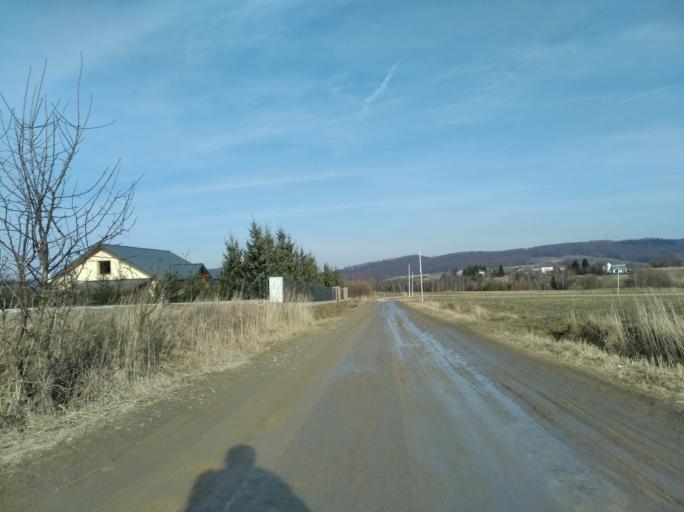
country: PL
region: Subcarpathian Voivodeship
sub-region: Powiat brzozowski
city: Grabownica Starzenska
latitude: 49.6503
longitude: 22.0637
